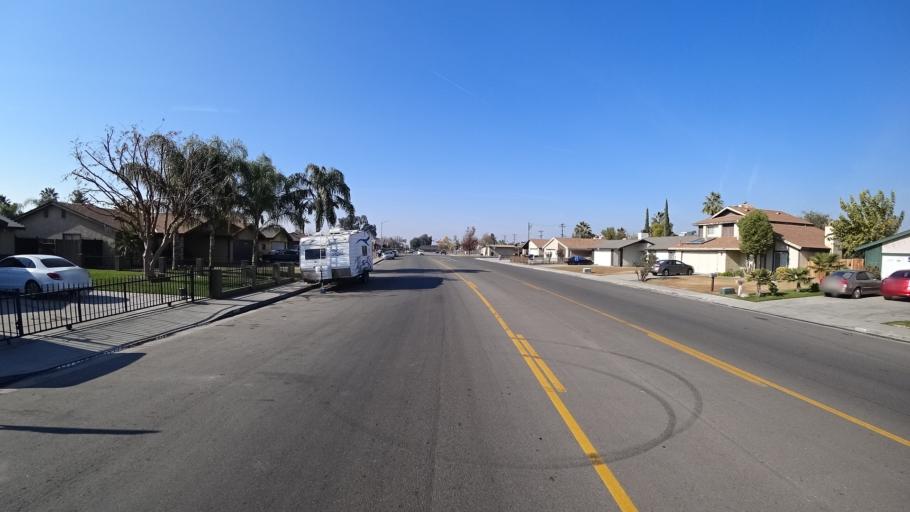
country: US
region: California
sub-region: Kern County
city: Greenfield
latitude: 35.3031
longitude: -119.0290
